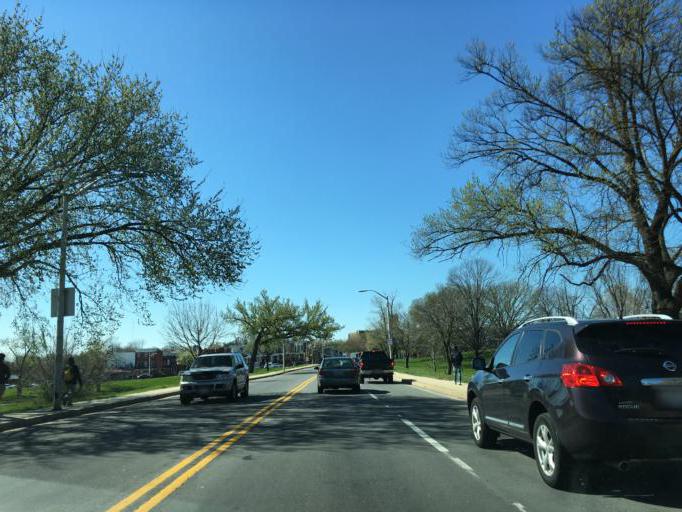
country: US
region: Maryland
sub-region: City of Baltimore
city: Baltimore
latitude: 39.3201
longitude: -76.5889
